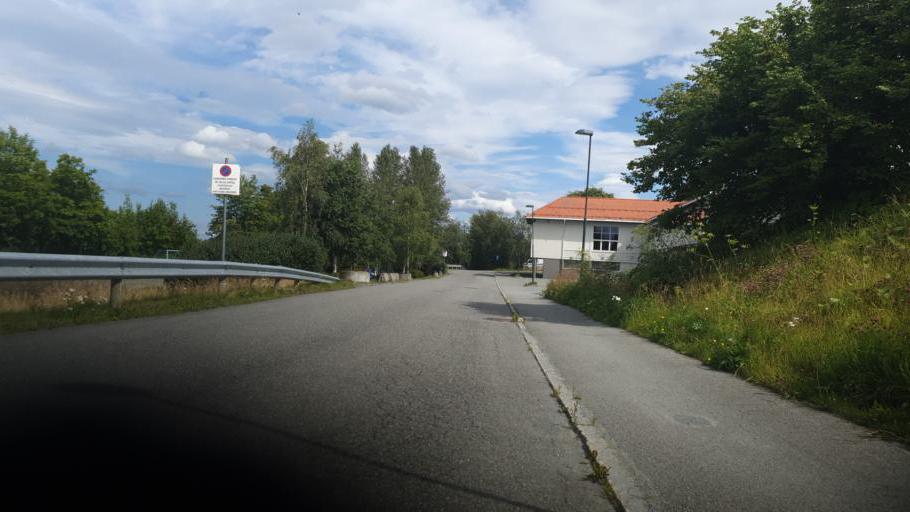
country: NO
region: Sor-Trondelag
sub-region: Malvik
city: Malvik
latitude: 63.4395
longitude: 10.6390
